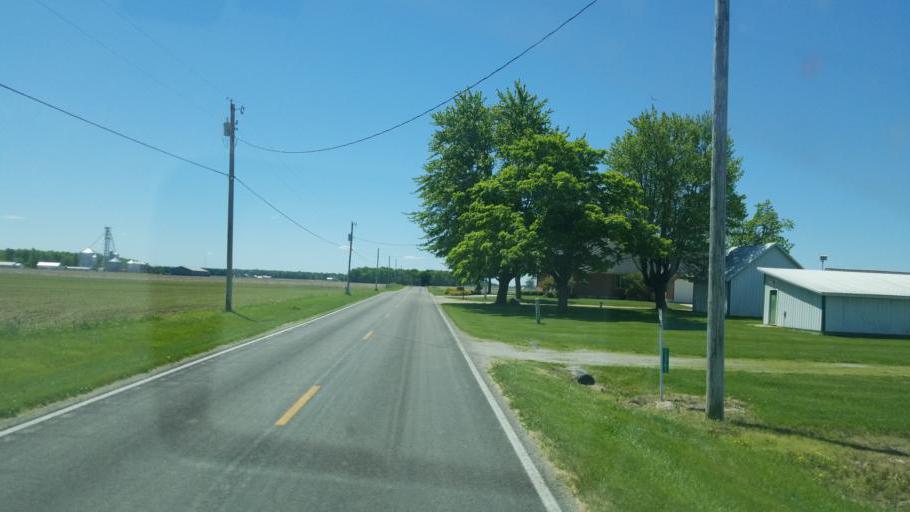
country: US
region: Ohio
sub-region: Shelby County
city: Fort Loramie
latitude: 40.3622
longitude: -84.3386
